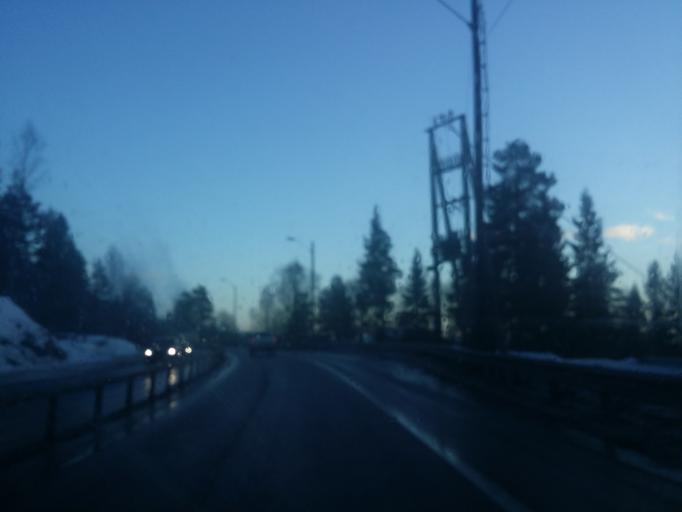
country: NO
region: Buskerud
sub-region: Hole
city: Vik
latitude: 59.9734
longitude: 10.3331
